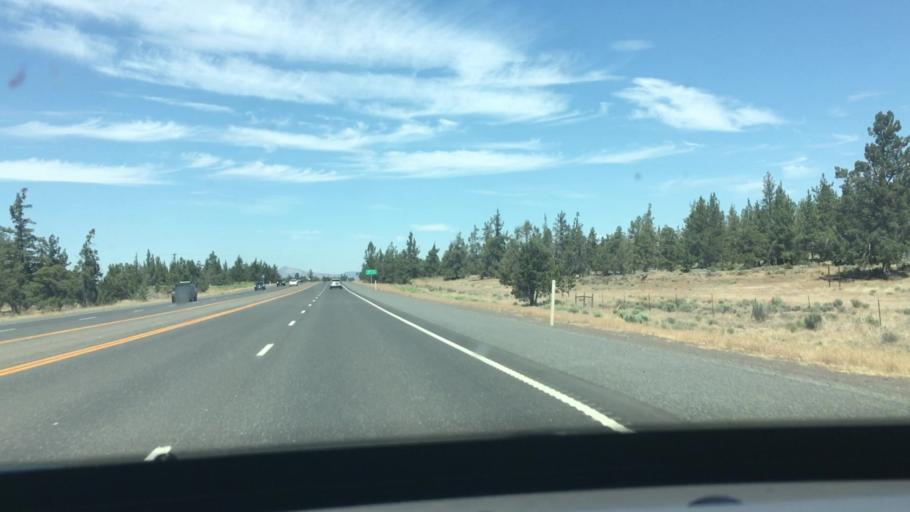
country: US
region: Oregon
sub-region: Deschutes County
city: Redmond
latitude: 44.1719
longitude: -121.2508
